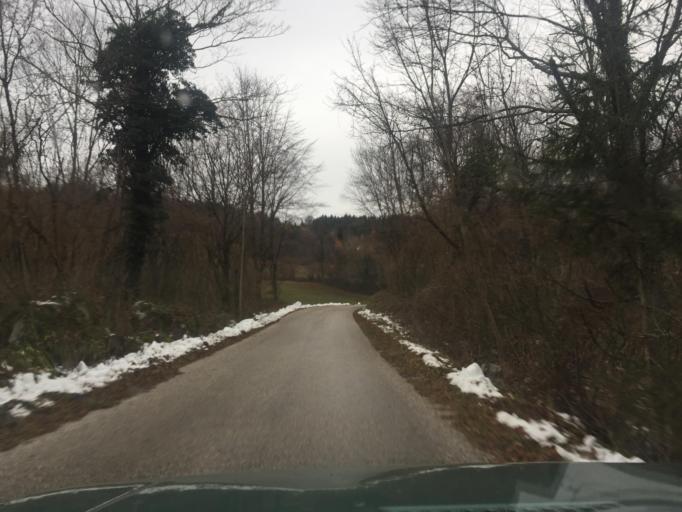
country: SI
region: Kanal
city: Kanal
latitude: 46.0642
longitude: 13.6625
